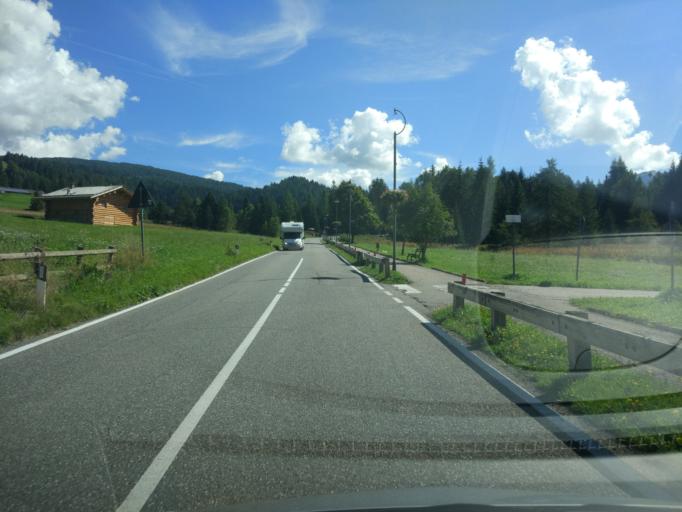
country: IT
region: Trentino-Alto Adige
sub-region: Provincia di Trento
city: Moena
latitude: 46.3122
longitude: 11.6669
